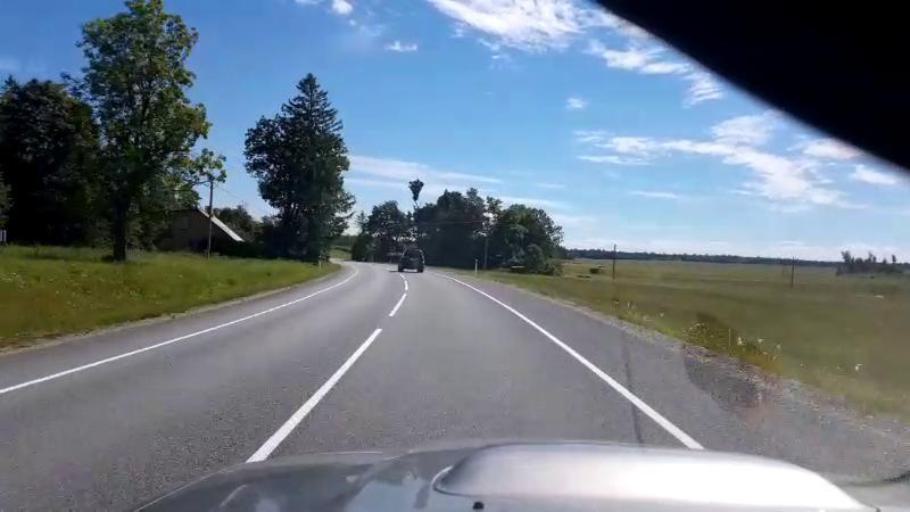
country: EE
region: Jaervamaa
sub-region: Jaerva-Jaani vald
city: Jarva-Jaani
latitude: 59.0240
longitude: 25.8978
